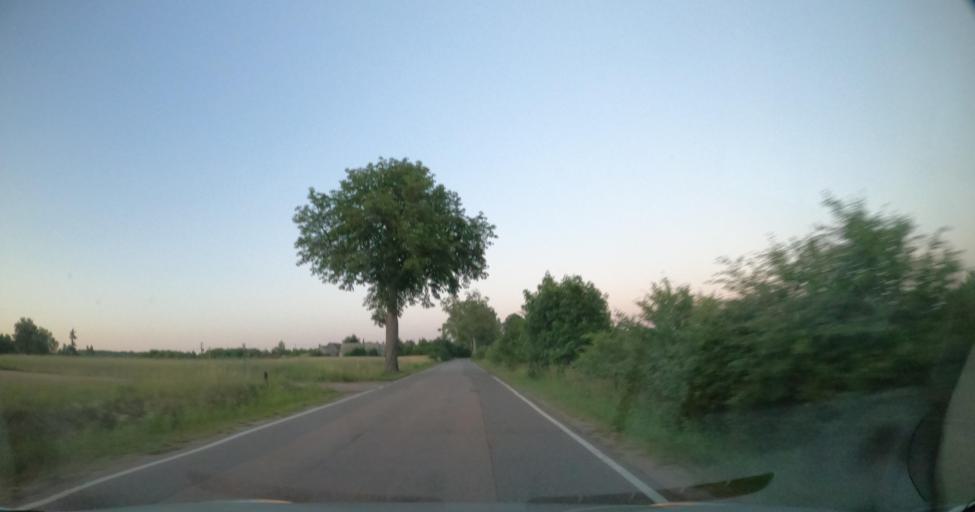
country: PL
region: Pomeranian Voivodeship
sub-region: Powiat wejherowski
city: Szemud
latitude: 54.4638
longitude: 18.1316
